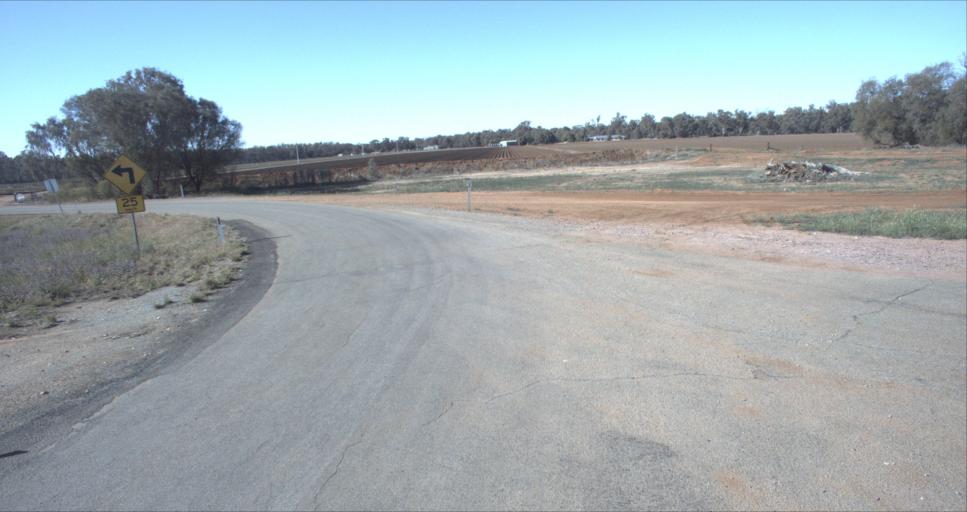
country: AU
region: New South Wales
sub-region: Leeton
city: Leeton
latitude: -34.6060
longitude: 146.2554
